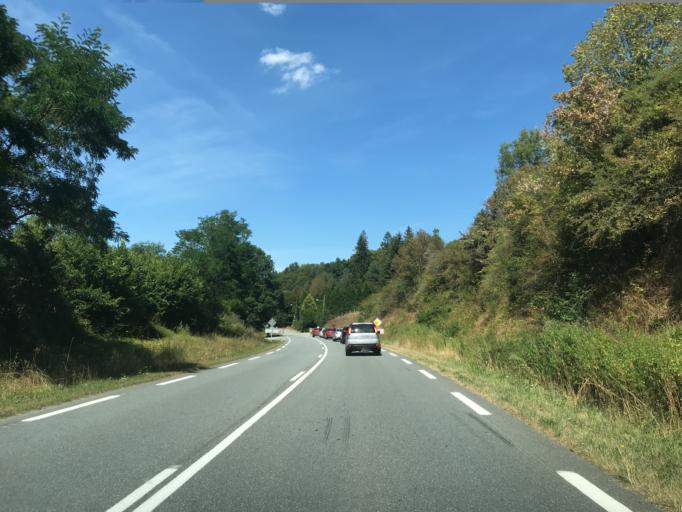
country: FR
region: Limousin
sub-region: Departement de la Creuse
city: Felletin
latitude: 45.9166
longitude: 2.1935
